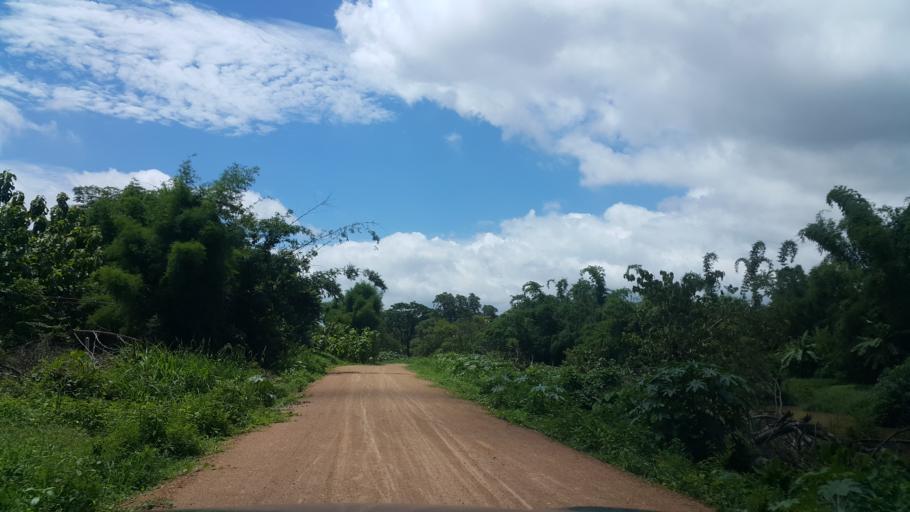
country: TH
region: Sukhothai
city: Thung Saliam
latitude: 17.3233
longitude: 99.5109
